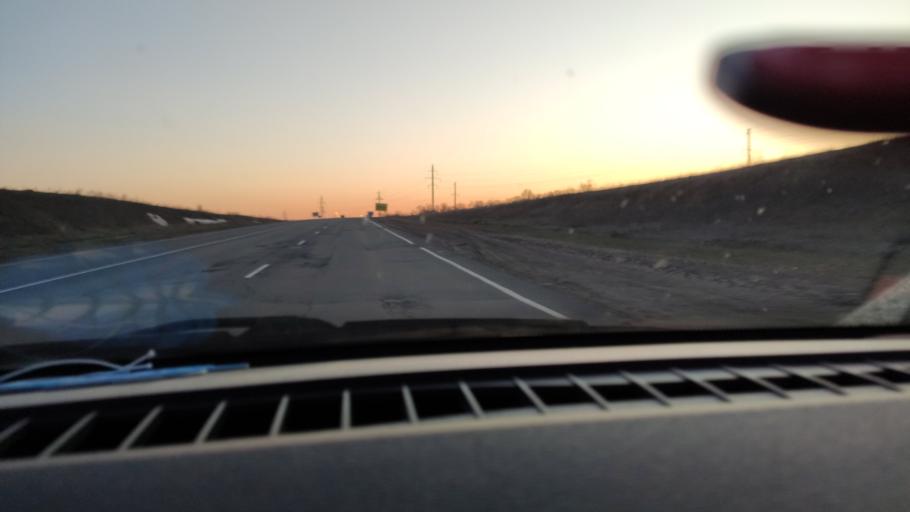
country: RU
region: Saratov
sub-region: Saratovskiy Rayon
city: Saratov
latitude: 51.7672
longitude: 46.0792
